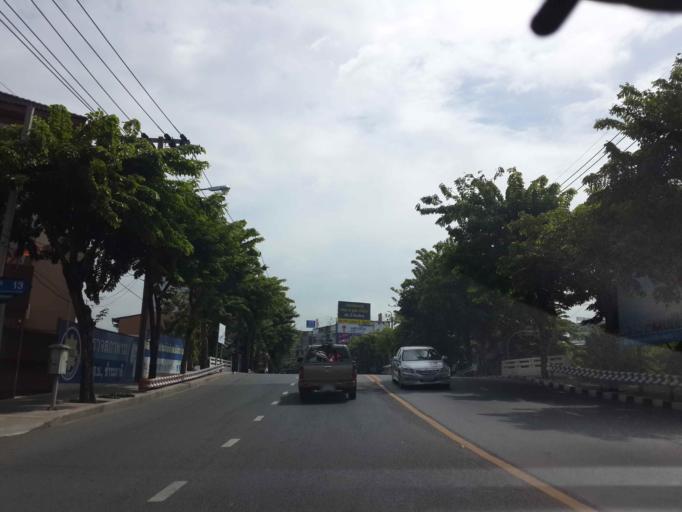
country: TH
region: Bangkok
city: Khan Na Yao
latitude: 13.8451
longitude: 100.6637
